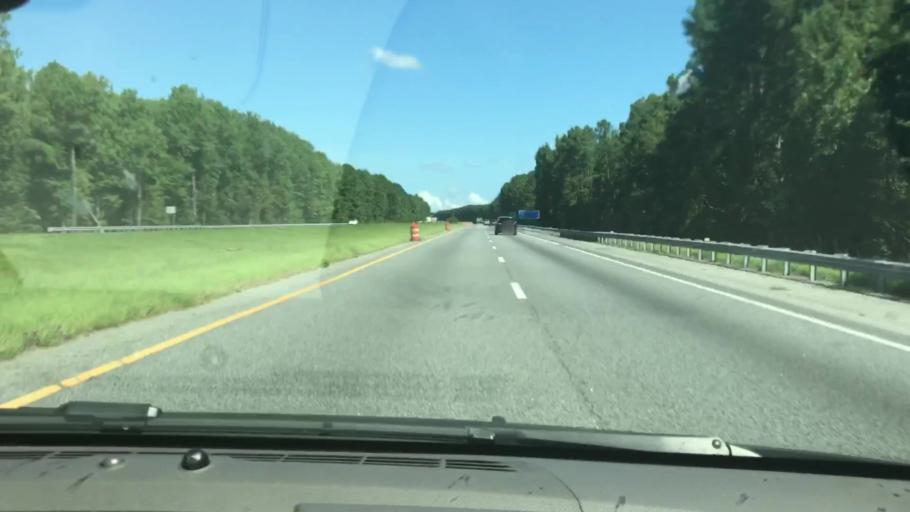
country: US
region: Georgia
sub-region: Harris County
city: Hamilton
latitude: 32.6415
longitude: -84.9697
